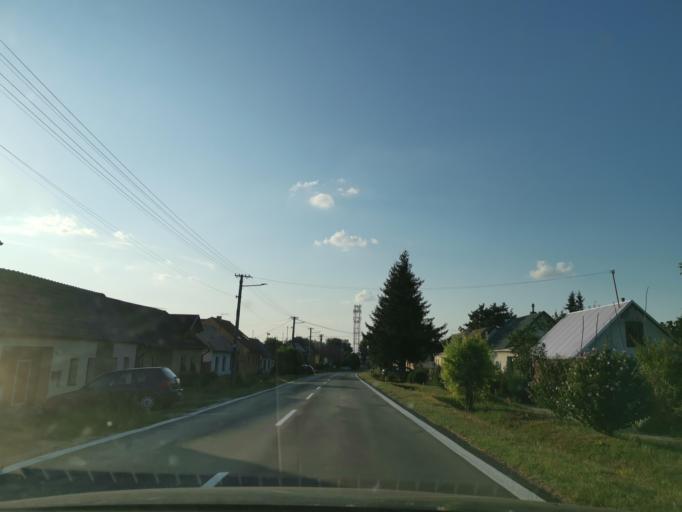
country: SK
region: Bratislavsky
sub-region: Okres Malacky
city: Malacky
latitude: 48.5069
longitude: 16.9985
